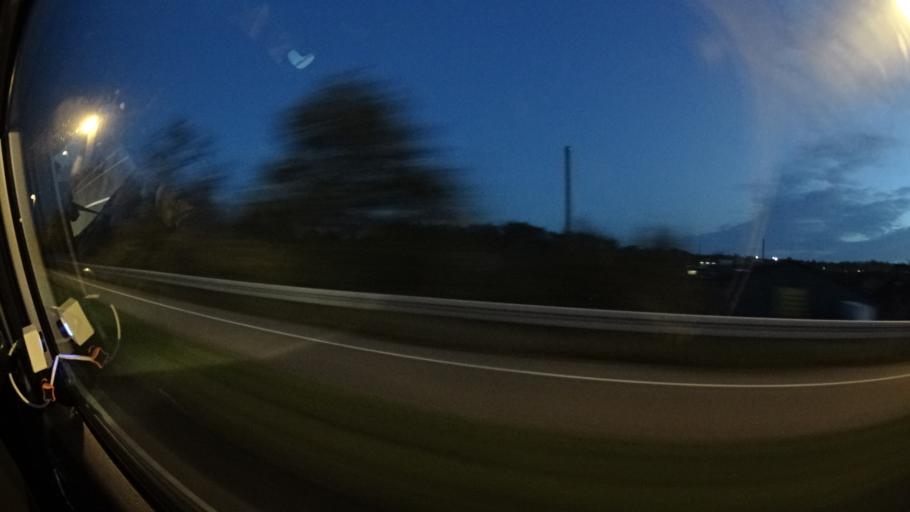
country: DK
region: South Denmark
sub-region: Odense Kommune
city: Hojby
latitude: 55.3469
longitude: 10.4444
